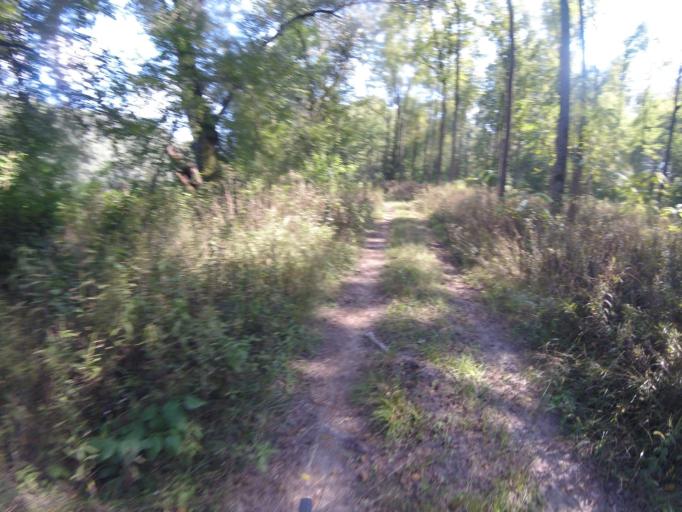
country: HU
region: Bacs-Kiskun
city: Baja
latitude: 46.1985
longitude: 18.8681
